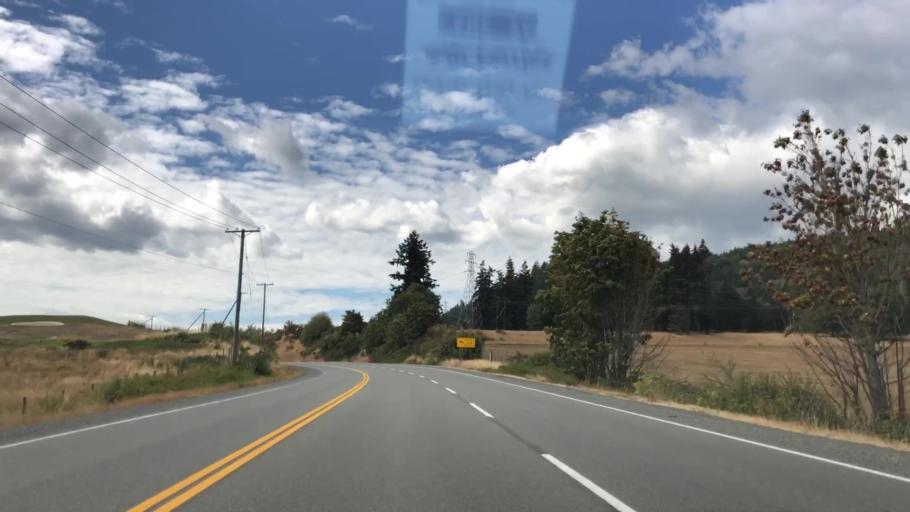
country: CA
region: British Columbia
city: Duncan
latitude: 48.8141
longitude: -123.7424
